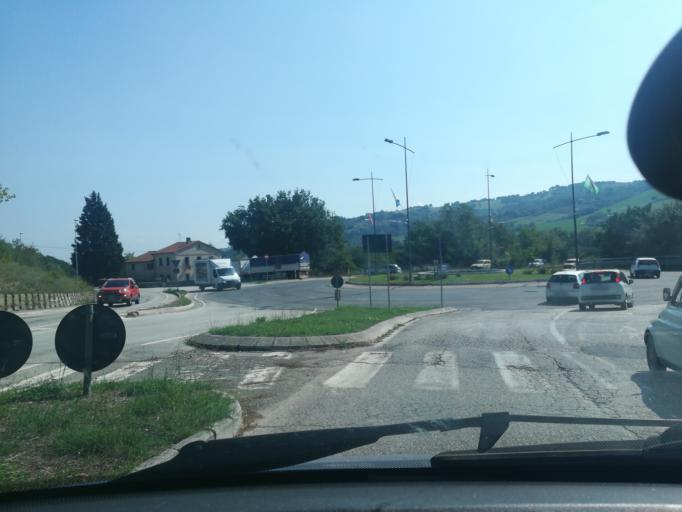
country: IT
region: The Marches
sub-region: Provincia di Macerata
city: Tolentino
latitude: 43.2142
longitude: 13.3053
